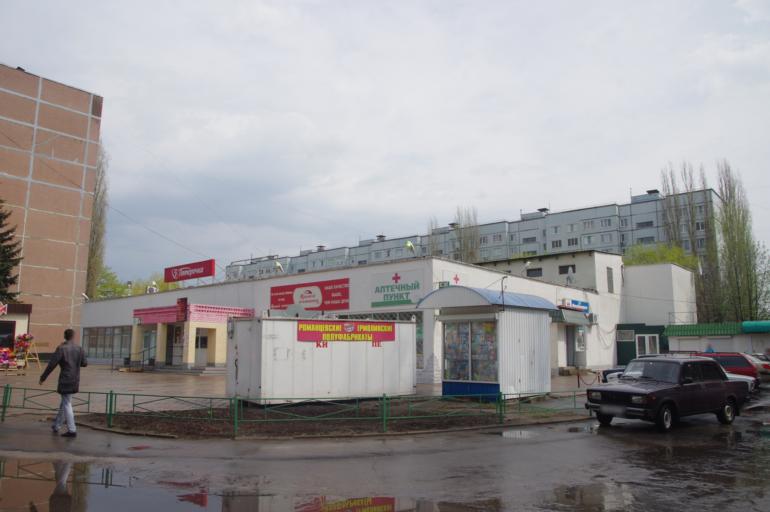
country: RU
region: Kursk
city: Kurchatov
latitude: 51.6566
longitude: 35.6717
